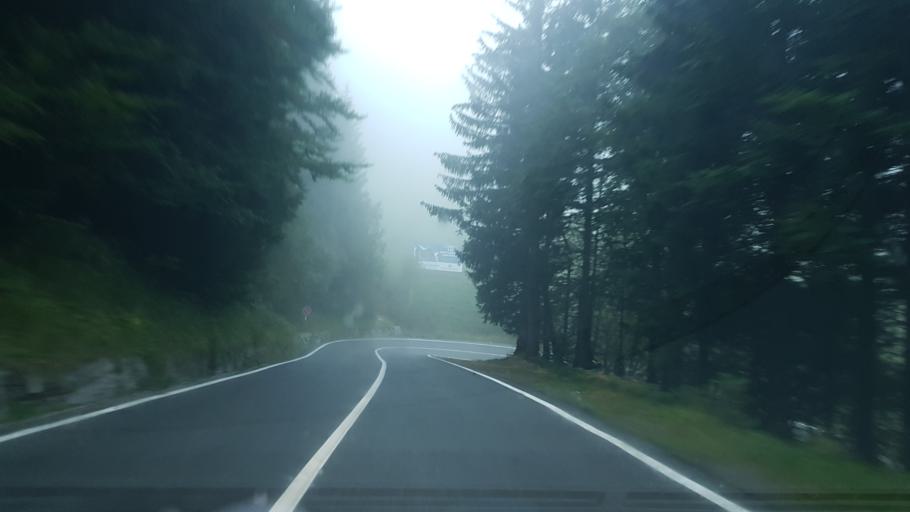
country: IT
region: Piedmont
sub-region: Provincia di Cuneo
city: Frabosa Soprana
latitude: 44.2575
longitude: 7.7756
